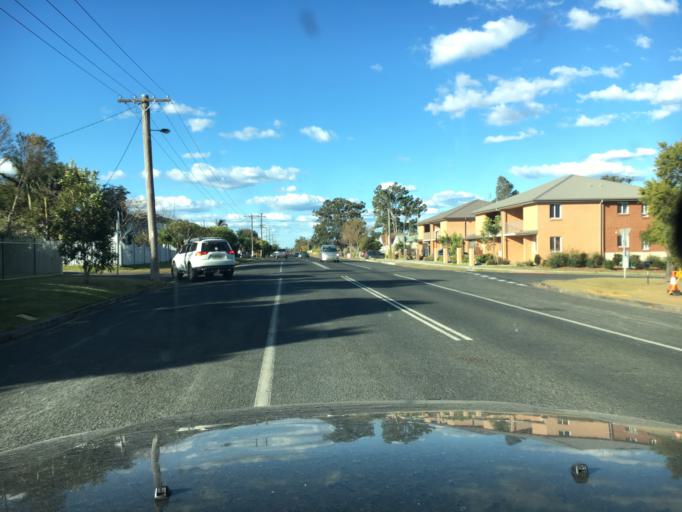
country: AU
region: New South Wales
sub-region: Maitland Municipality
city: East Maitland
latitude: -32.7571
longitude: 151.5843
